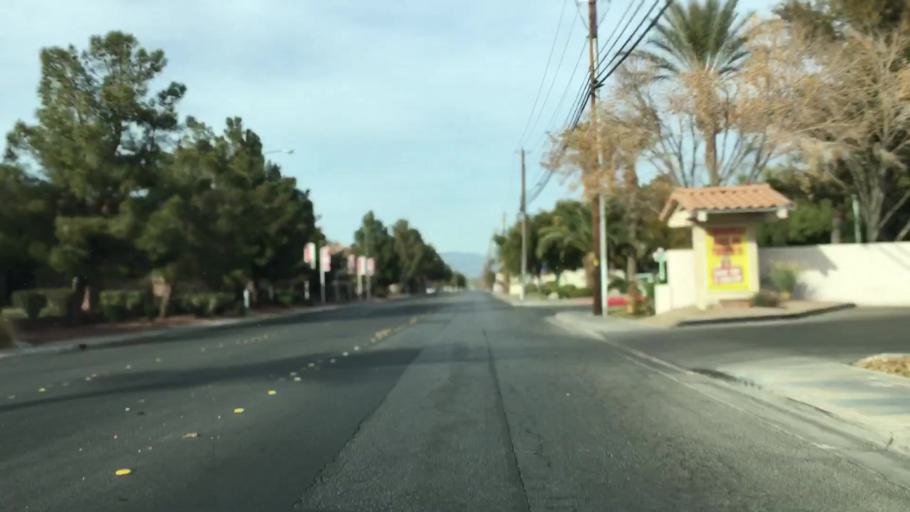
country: US
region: Nevada
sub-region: Clark County
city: Whitney
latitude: 36.0718
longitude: -115.0871
